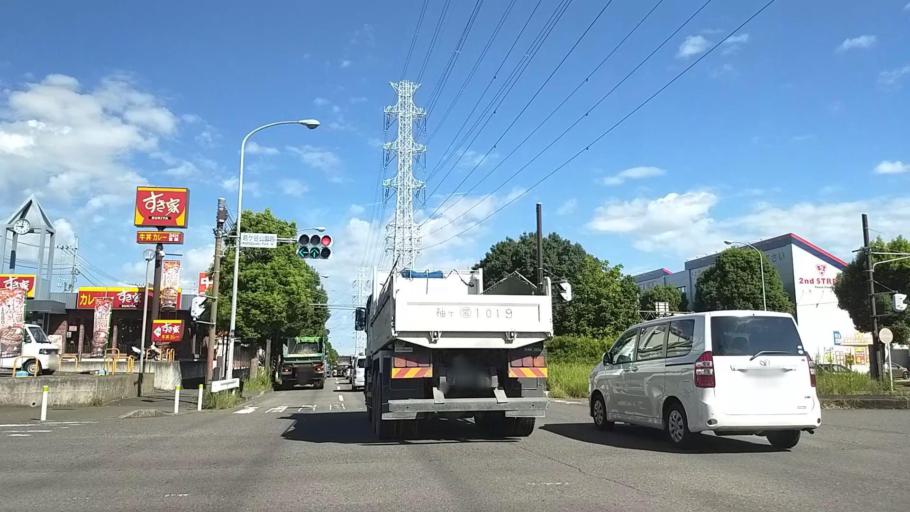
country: JP
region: Tokyo
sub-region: Machida-shi
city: Machida
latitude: 35.5392
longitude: 139.5631
